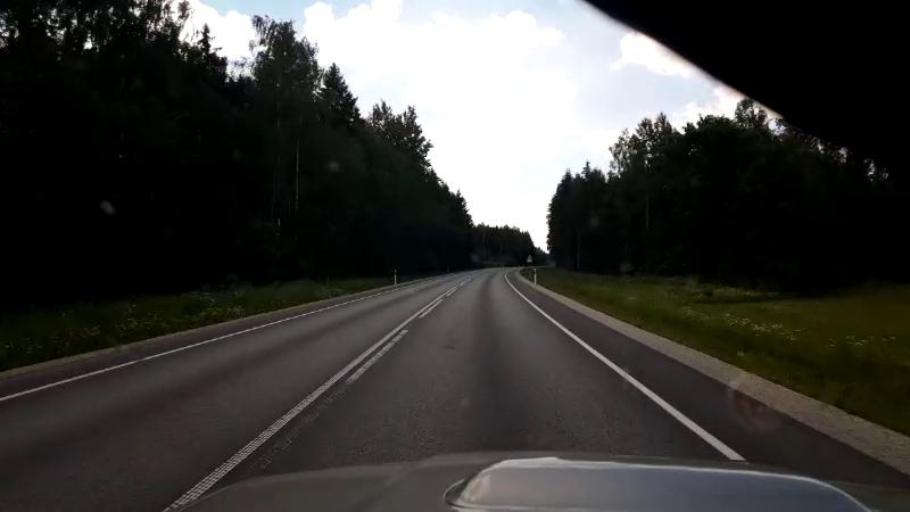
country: EE
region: Jaervamaa
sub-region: Paide linn
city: Paide
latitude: 58.9701
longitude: 25.6637
